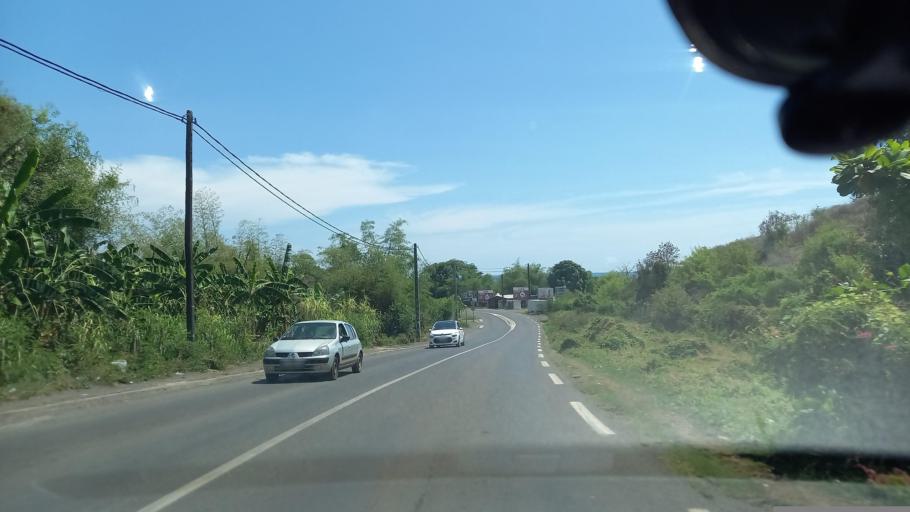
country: YT
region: Mamoudzou
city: Mamoudzou
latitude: -12.7583
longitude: 45.2313
